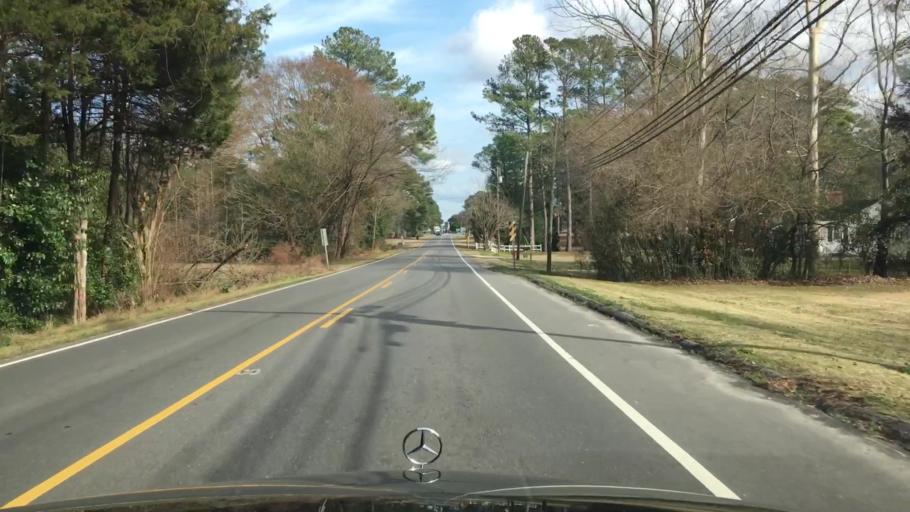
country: US
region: North Carolina
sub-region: Duplin County
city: Warsaw
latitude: 35.0011
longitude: -78.0850
